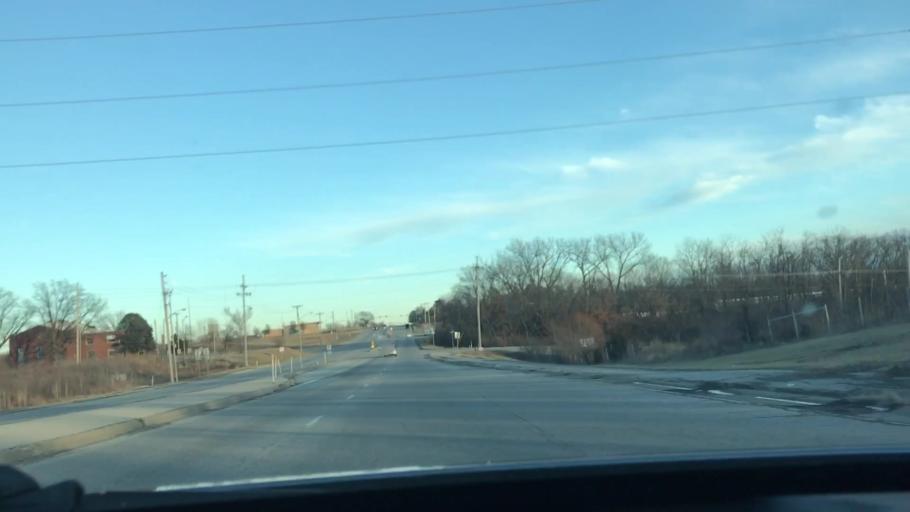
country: US
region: Kansas
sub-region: Wyandotte County
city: Edwardsville
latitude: 39.1163
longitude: -94.8086
